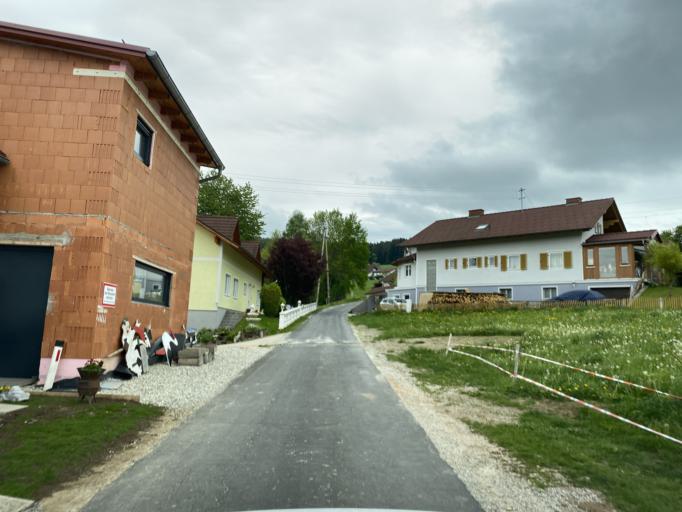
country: AT
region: Styria
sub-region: Politischer Bezirk Weiz
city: Gschaid bei Birkfeld
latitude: 47.3628
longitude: 15.7285
